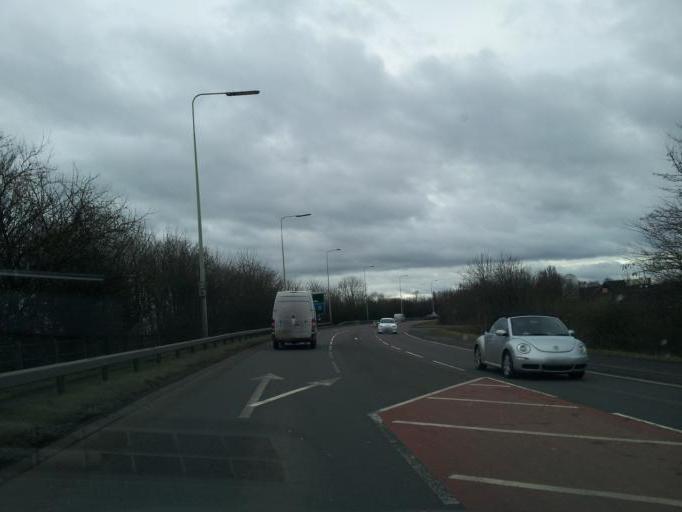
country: GB
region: England
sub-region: Staffordshire
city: Stafford
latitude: 52.7665
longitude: -2.1063
